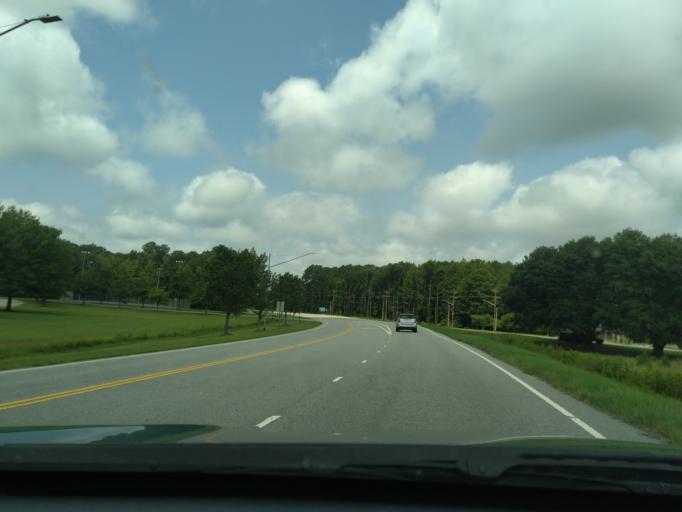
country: US
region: North Carolina
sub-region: Edgecombe County
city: Tarboro
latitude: 35.9259
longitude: -77.5685
